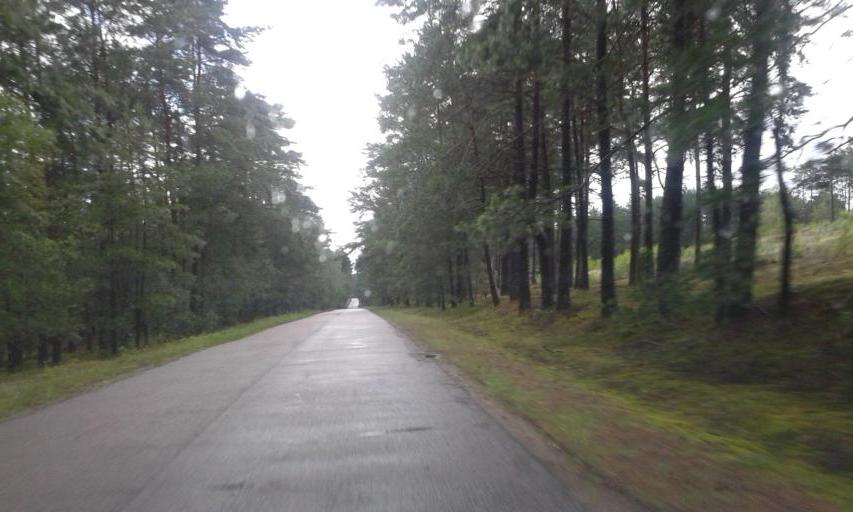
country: PL
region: West Pomeranian Voivodeship
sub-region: Powiat szczecinecki
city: Borne Sulinowo
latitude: 53.5463
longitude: 16.5127
